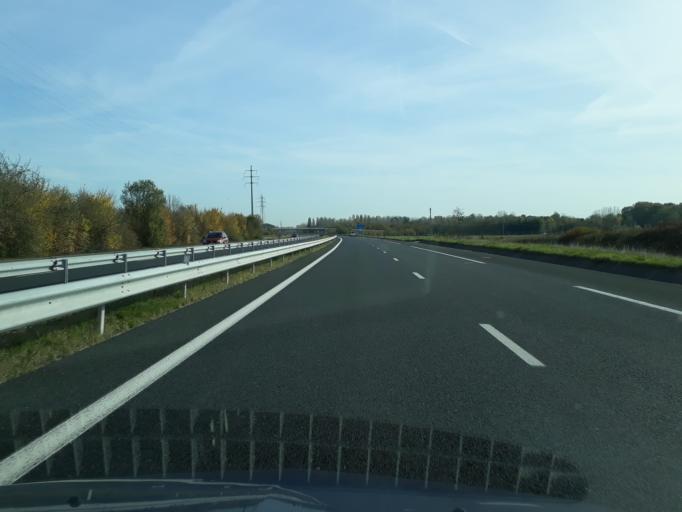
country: FR
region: Champagne-Ardenne
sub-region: Departement de l'Aube
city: Saint-Pouange
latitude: 48.2352
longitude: 4.0241
